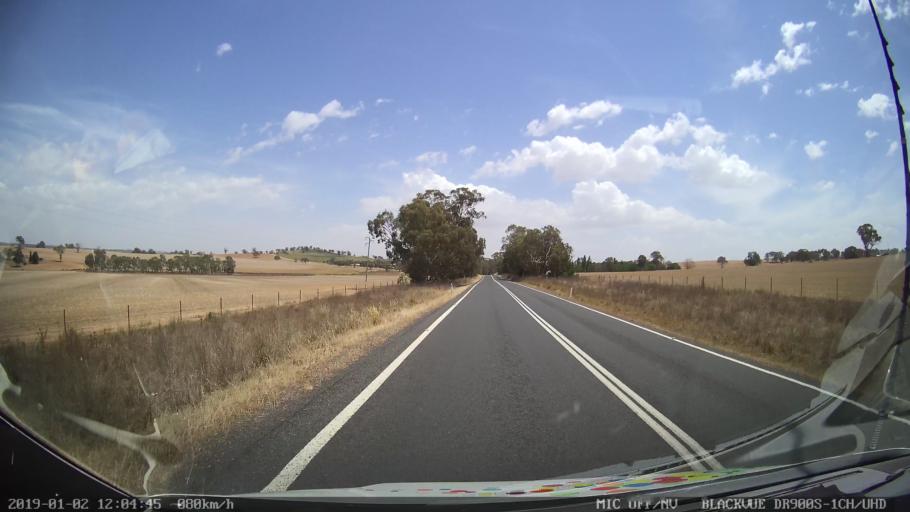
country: AU
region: New South Wales
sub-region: Young
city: Young
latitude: -34.5218
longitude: 148.3071
